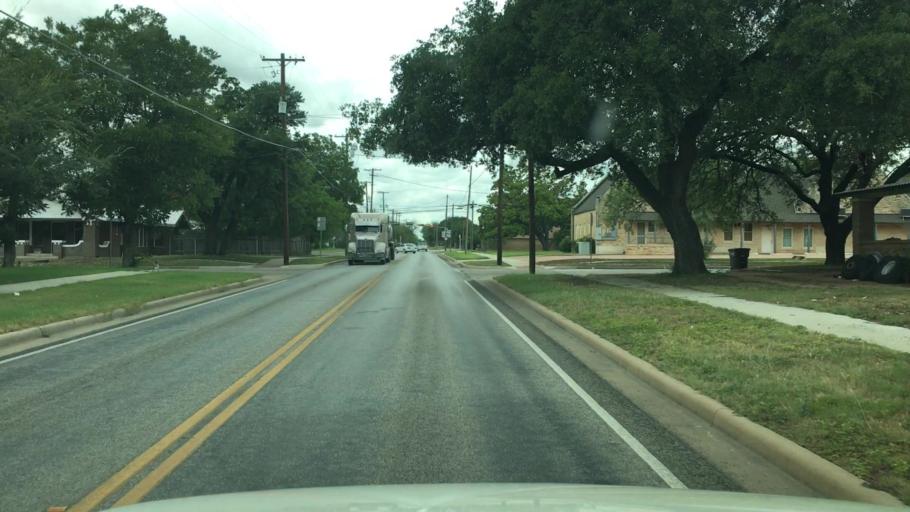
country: US
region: Texas
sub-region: McCulloch County
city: Brady
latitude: 31.1262
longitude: -99.3329
